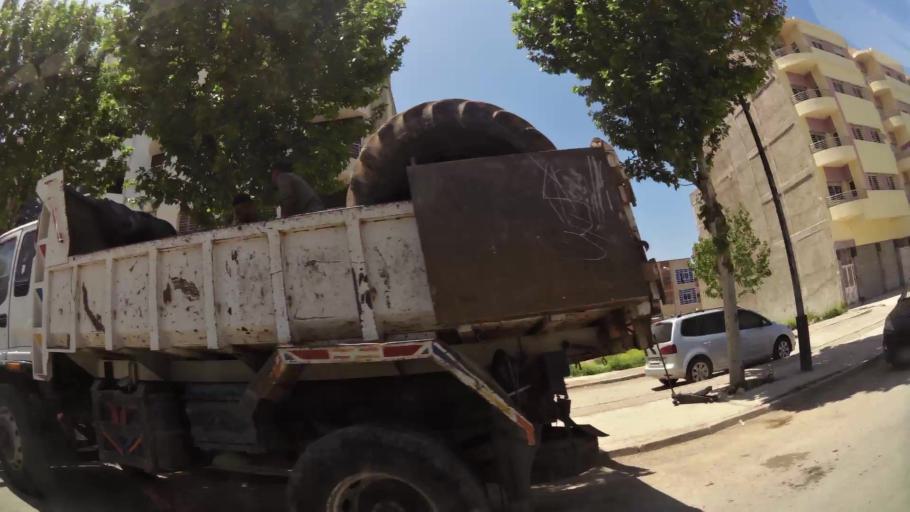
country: MA
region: Fes-Boulemane
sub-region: Fes
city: Fes
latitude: 34.0218
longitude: -5.0545
